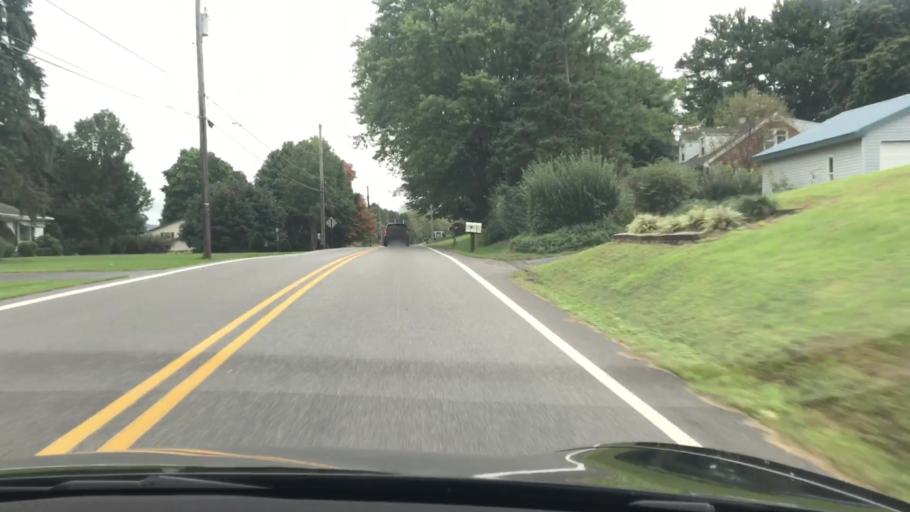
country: US
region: Pennsylvania
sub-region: York County
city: Dillsburg
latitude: 40.0789
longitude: -77.0805
